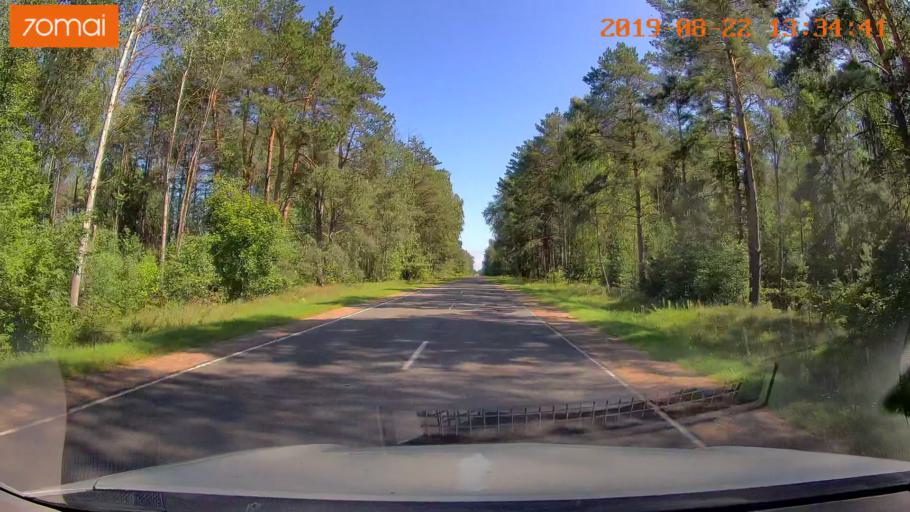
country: BY
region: Minsk
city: Staryya Darohi
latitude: 53.2149
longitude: 28.2478
